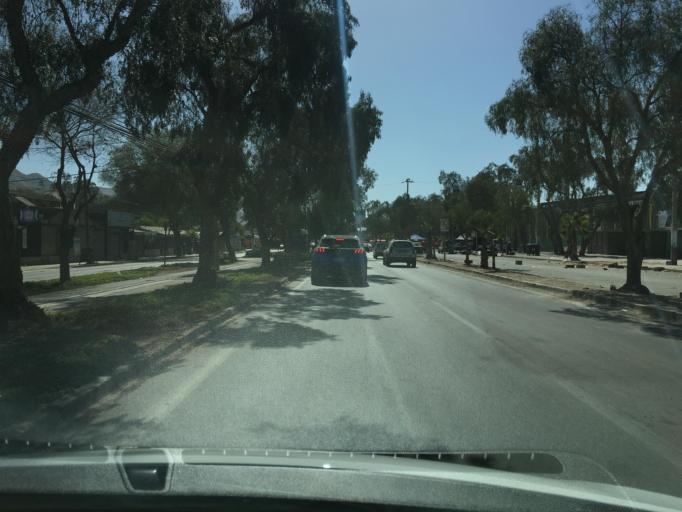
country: CL
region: Atacama
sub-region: Provincia de Copiapo
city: Copiapo
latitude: -27.3779
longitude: -70.3207
